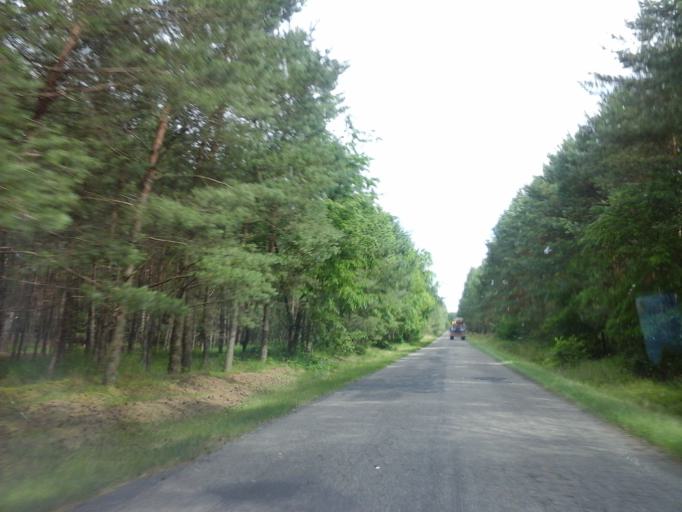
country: PL
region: West Pomeranian Voivodeship
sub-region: Powiat stargardzki
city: Kobylanka
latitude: 53.4539
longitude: 14.8654
